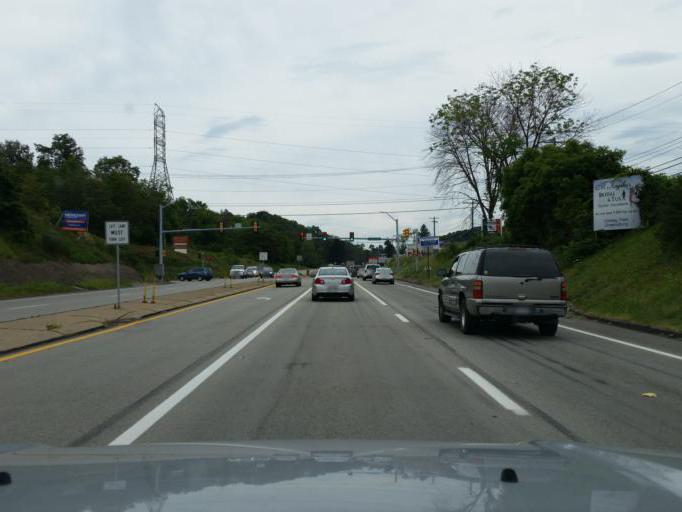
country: US
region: Pennsylvania
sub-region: Westmoreland County
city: Greensburg
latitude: 40.2974
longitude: -79.4804
